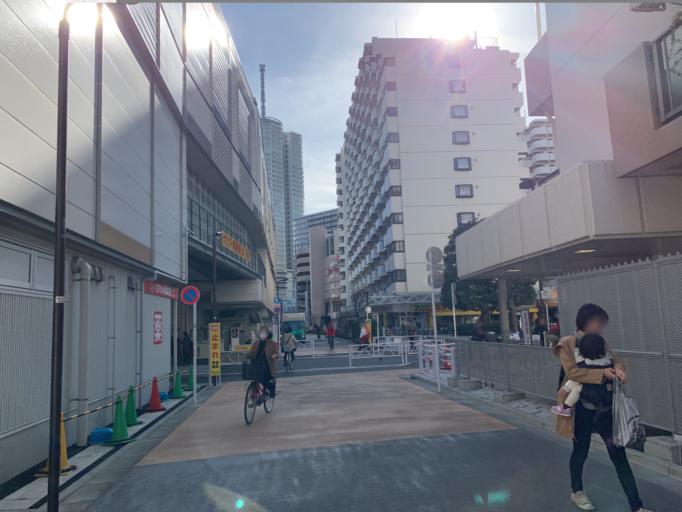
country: JP
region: Tokyo
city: Urayasu
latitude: 35.7183
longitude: 139.8196
